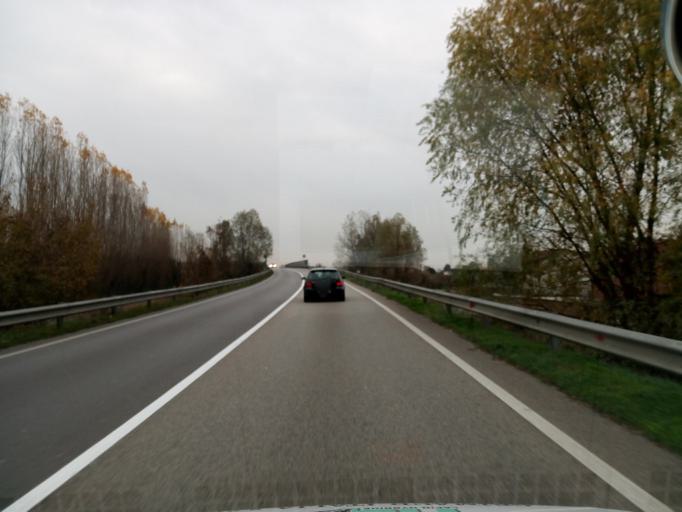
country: IT
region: Veneto
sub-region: Provincia di Padova
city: Saonara
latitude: 45.3580
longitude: 12.0040
